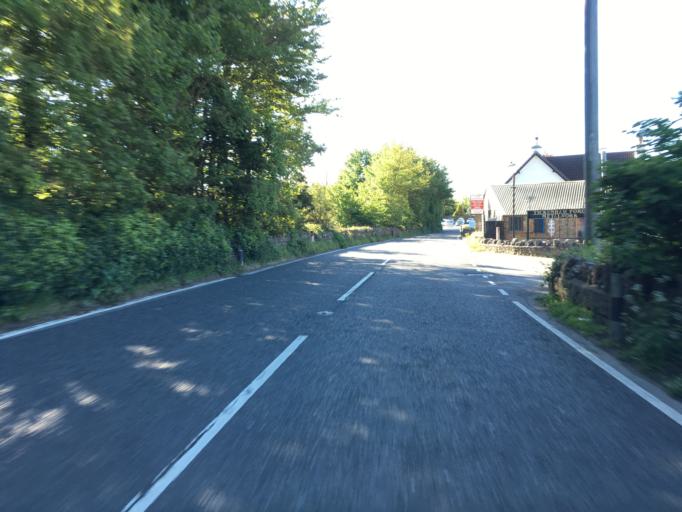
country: GB
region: England
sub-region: North Somerset
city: Nailsea
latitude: 51.4432
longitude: -2.7766
